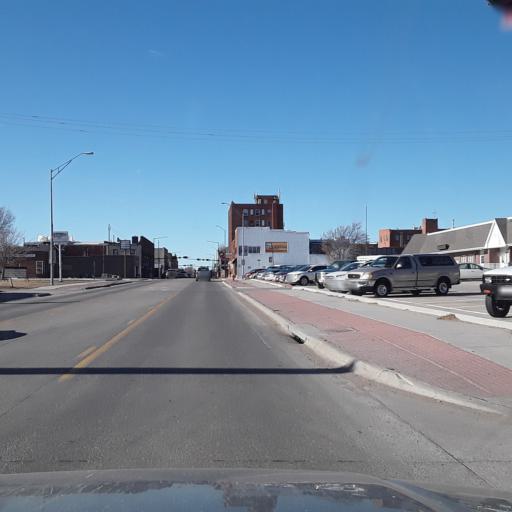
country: US
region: Nebraska
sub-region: Phelps County
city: Holdrege
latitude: 40.4381
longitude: -99.3670
